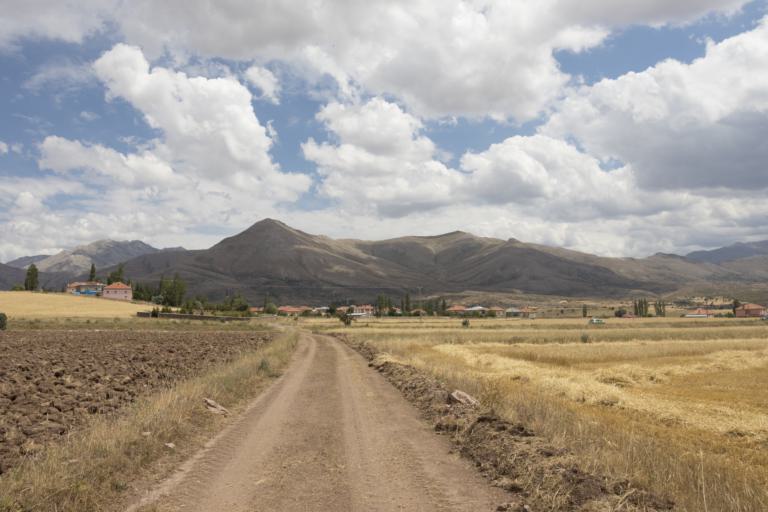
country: TR
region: Kayseri
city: Toklar
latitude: 38.4112
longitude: 36.0762
